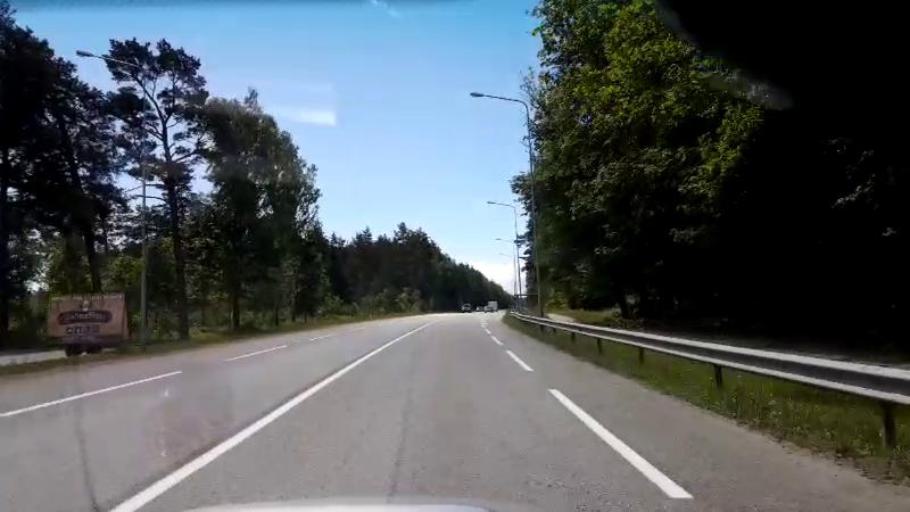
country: LV
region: Saulkrastu
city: Saulkrasti
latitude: 57.4632
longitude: 24.4341
